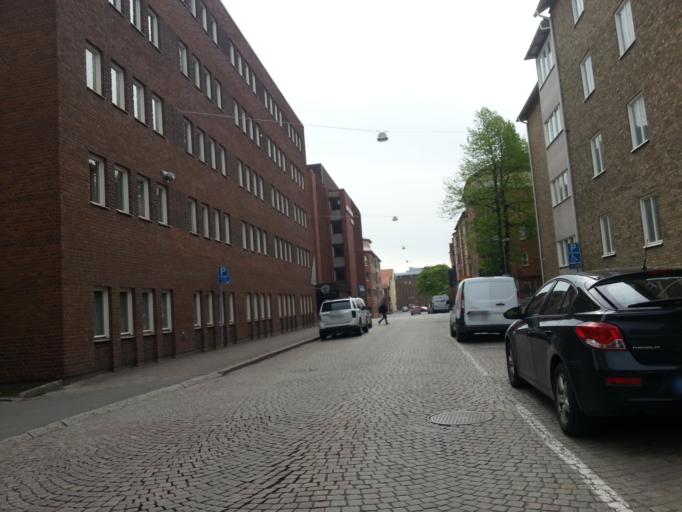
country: SE
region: Joenkoeping
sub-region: Jonkopings Kommun
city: Jonkoping
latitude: 57.7806
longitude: 14.1608
